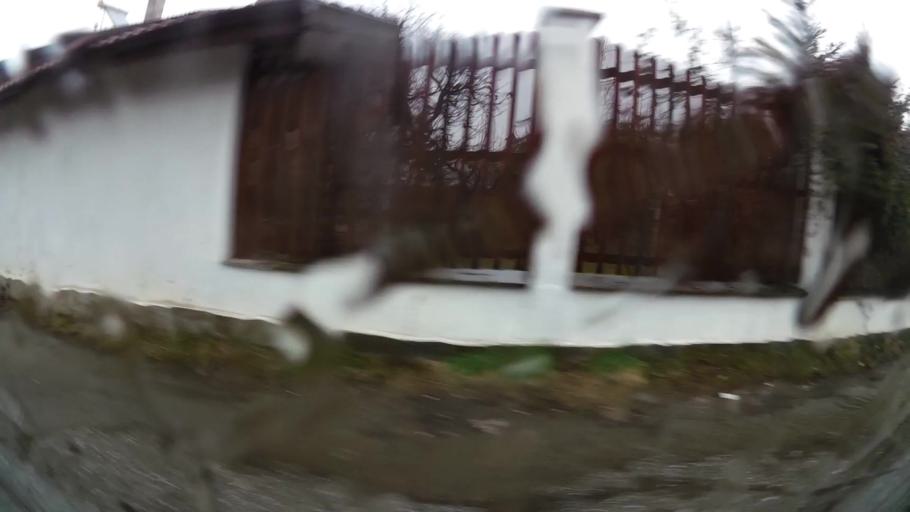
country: BG
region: Sofia-Capital
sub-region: Stolichna Obshtina
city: Sofia
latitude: 42.6286
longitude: 23.3662
